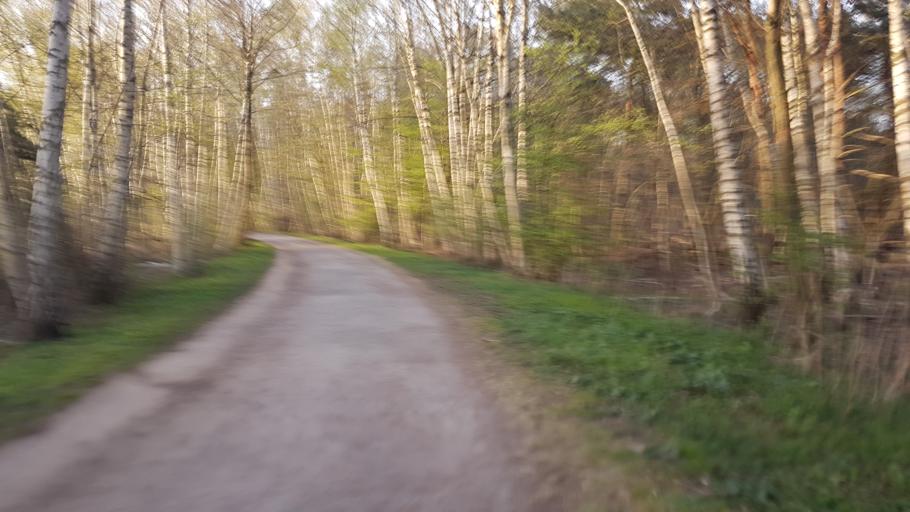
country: DE
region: Lower Saxony
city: Isernhagen Farster Bauerschaft
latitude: 52.4261
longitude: 9.8641
